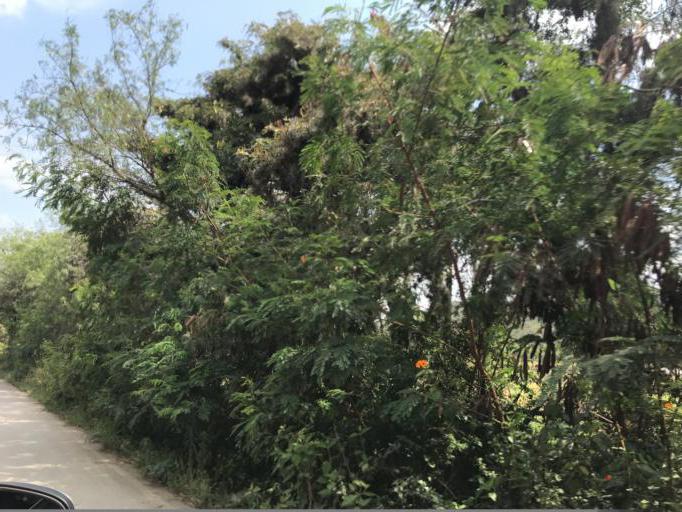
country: CO
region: Boyaca
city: Villa de Leiva
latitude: 5.6557
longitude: -73.5792
